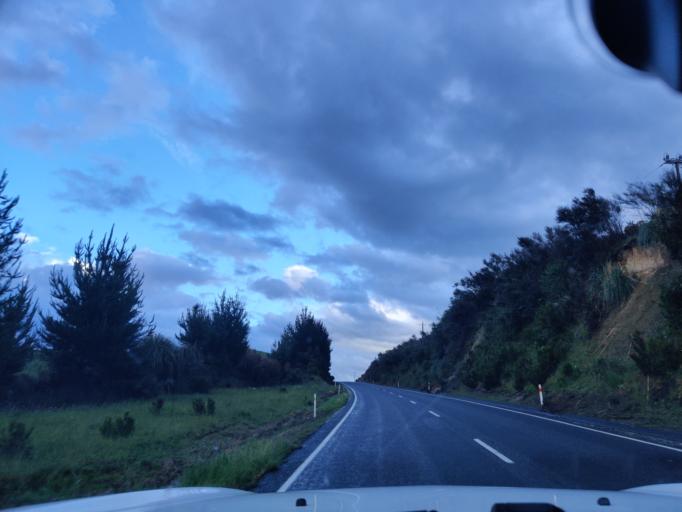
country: NZ
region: Waikato
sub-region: South Waikato District
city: Tokoroa
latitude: -38.3752
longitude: 175.7922
